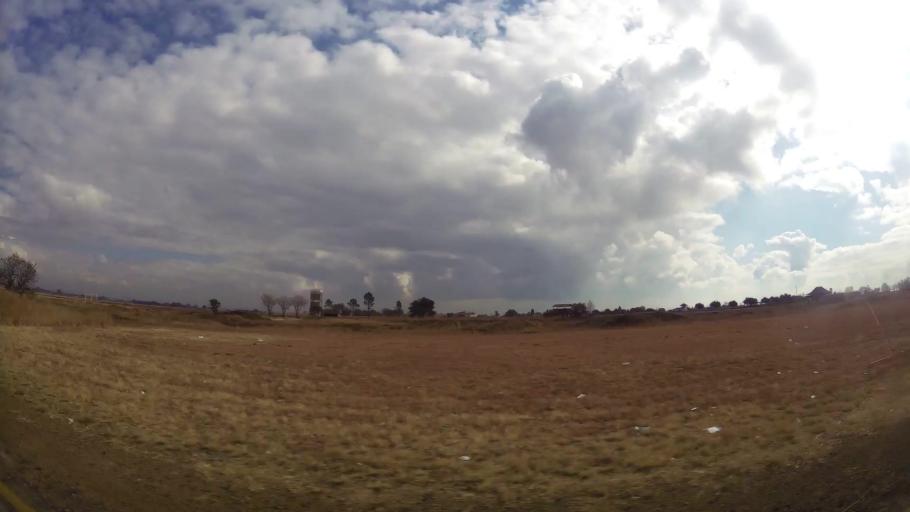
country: ZA
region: Gauteng
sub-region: Sedibeng District Municipality
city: Meyerton
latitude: -26.6182
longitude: 28.0586
